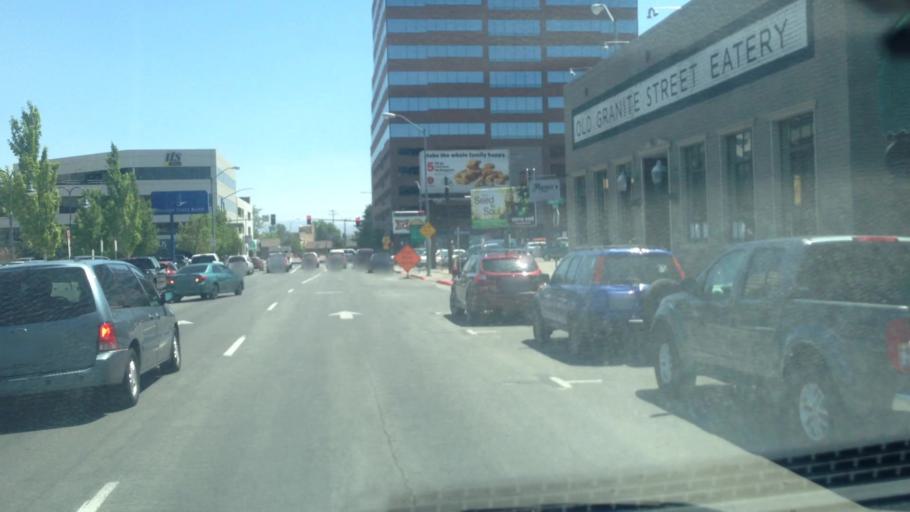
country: US
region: Nevada
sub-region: Washoe County
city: Reno
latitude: 39.5227
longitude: -119.8129
